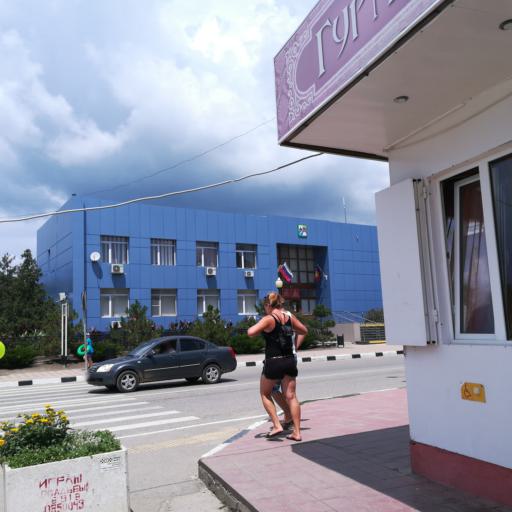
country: RU
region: Krasnodarskiy
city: Taman'
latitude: 45.2159
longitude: 36.7196
